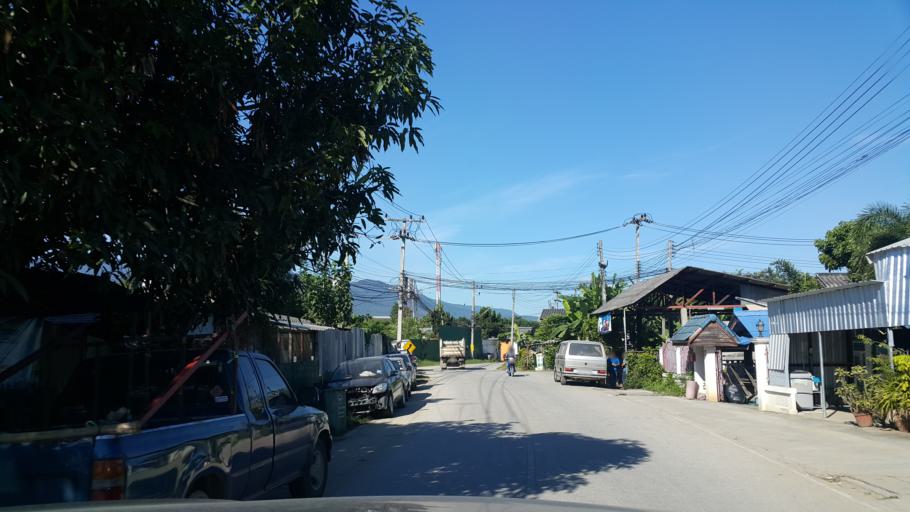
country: TH
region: Chiang Mai
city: San Sai
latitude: 18.8471
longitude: 98.9940
